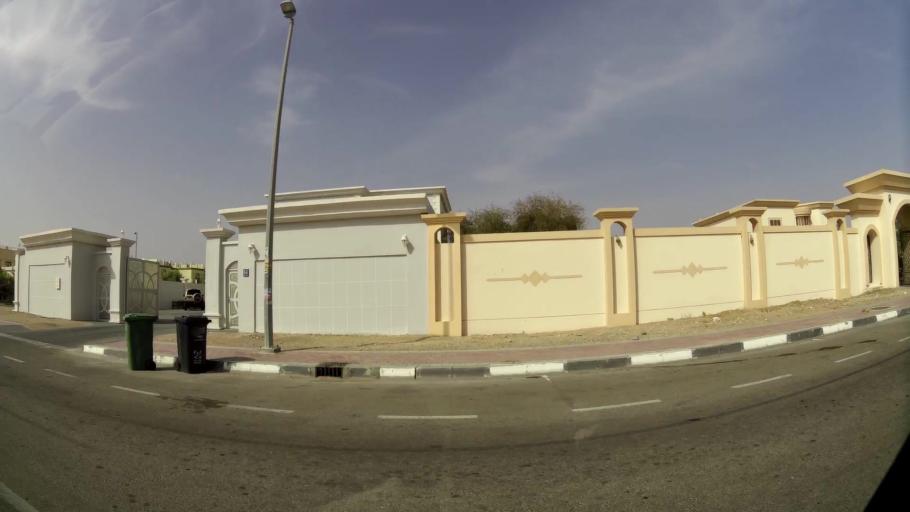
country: AE
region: Abu Dhabi
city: Al Ain
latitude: 24.1441
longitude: 55.7016
